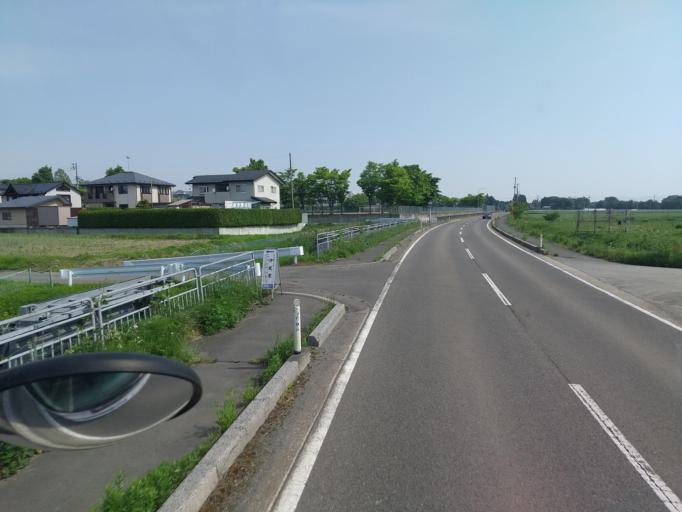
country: JP
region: Iwate
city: Hanamaki
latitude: 39.3902
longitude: 141.0875
